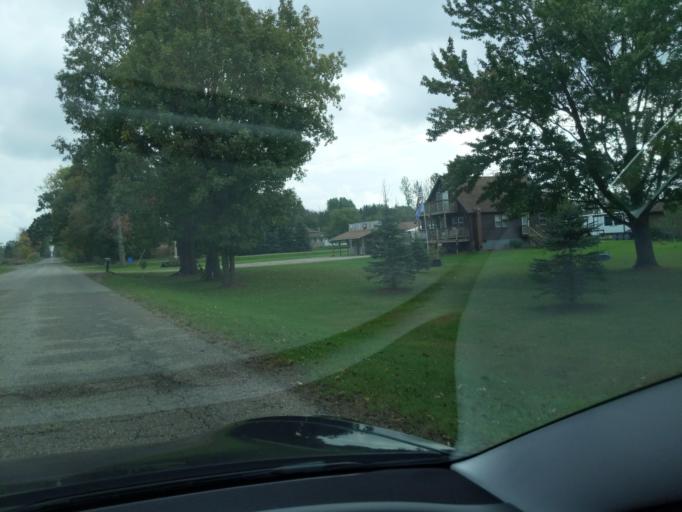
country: US
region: Michigan
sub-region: Eaton County
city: Eaton Rapids
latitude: 42.4908
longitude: -84.6513
